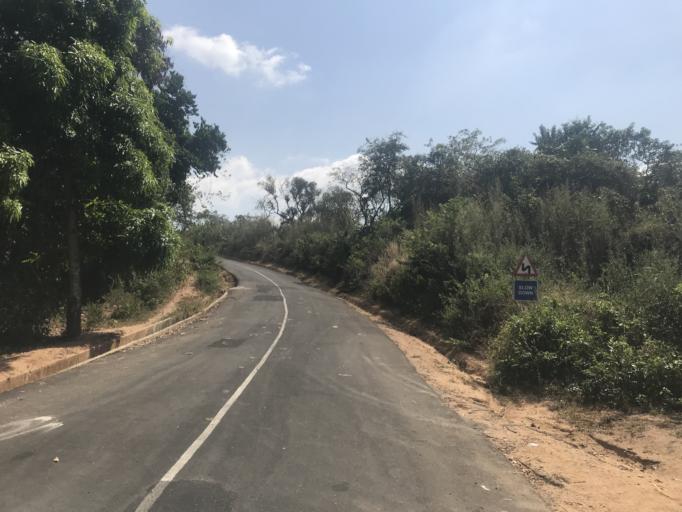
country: NG
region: Osun
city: Otan Ayegbaju
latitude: 7.8984
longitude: 4.8333
